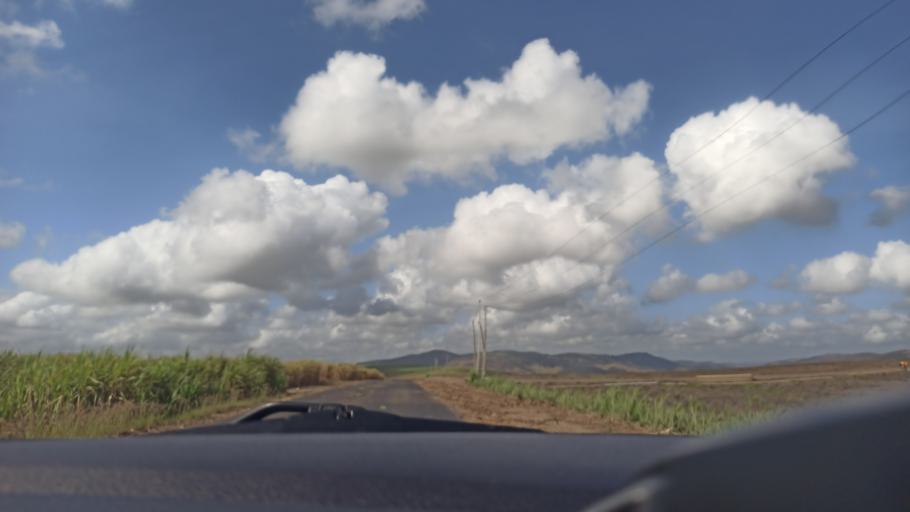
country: BR
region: Paraiba
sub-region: Juripiranga
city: Juripiranga
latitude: -7.3890
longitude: -35.2530
